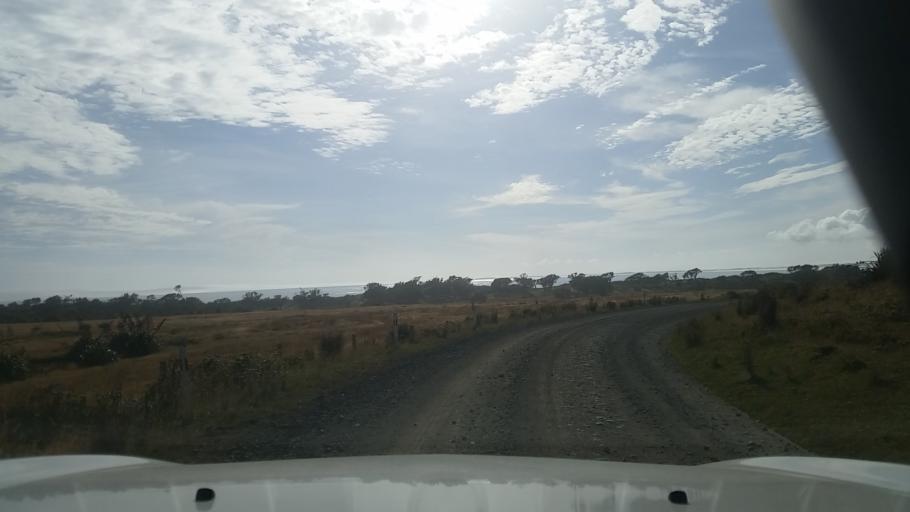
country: NZ
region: Chatham Islands
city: Waitangi
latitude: -43.7274
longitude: -176.5025
